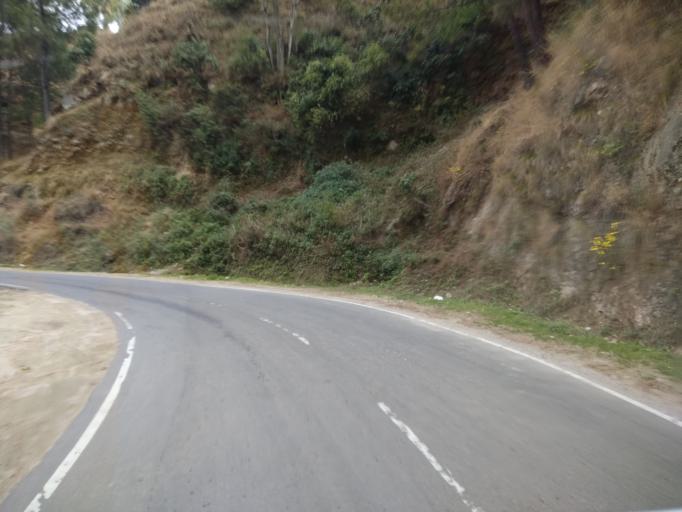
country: IN
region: Himachal Pradesh
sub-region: Kangra
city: Palampur
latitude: 32.1094
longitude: 76.4879
